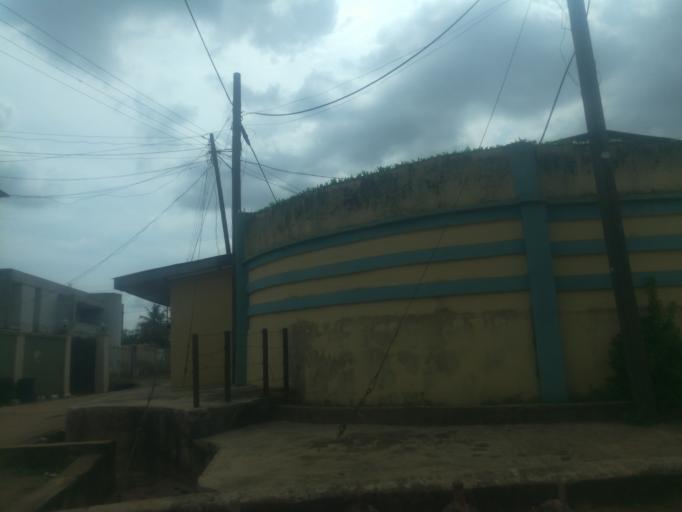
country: NG
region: Oyo
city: Ibadan
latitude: 7.4074
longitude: 3.9299
